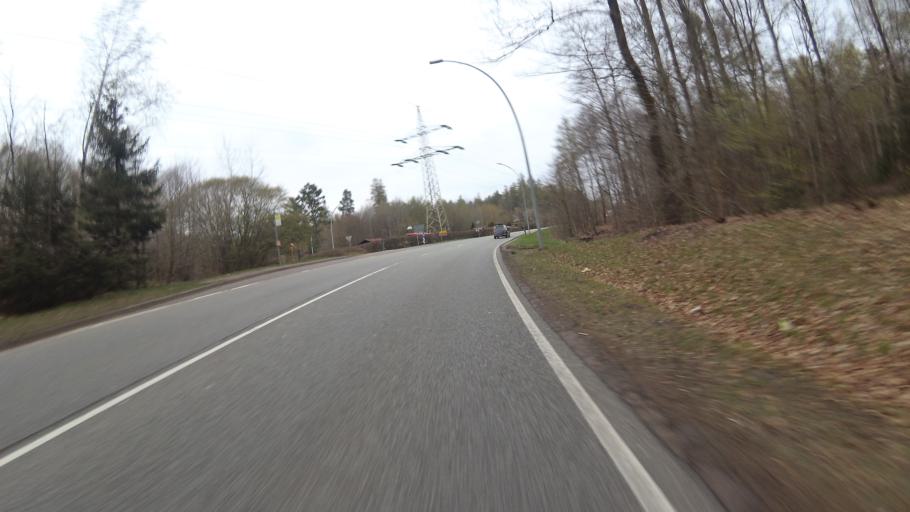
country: DE
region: Saarland
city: Sankt Ingbert
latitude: 49.2982
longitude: 7.1134
